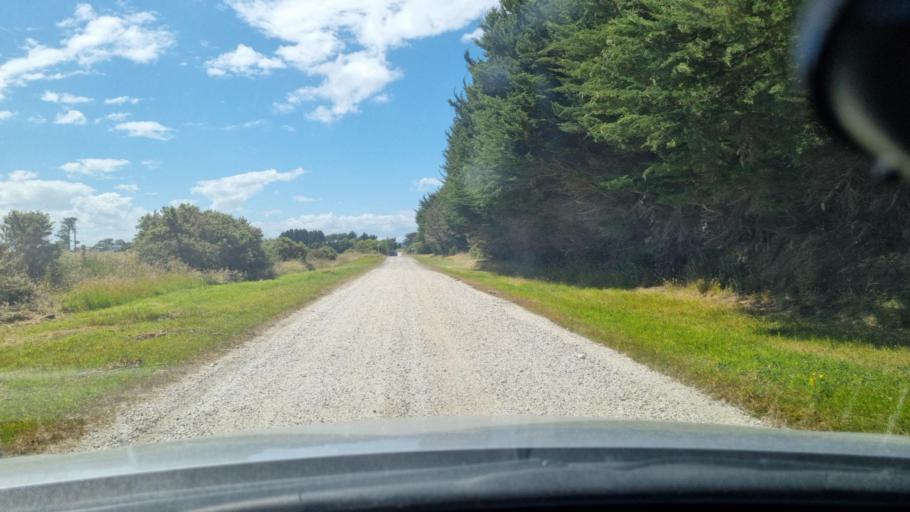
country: NZ
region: Southland
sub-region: Invercargill City
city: Invercargill
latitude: -46.4374
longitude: 168.3896
